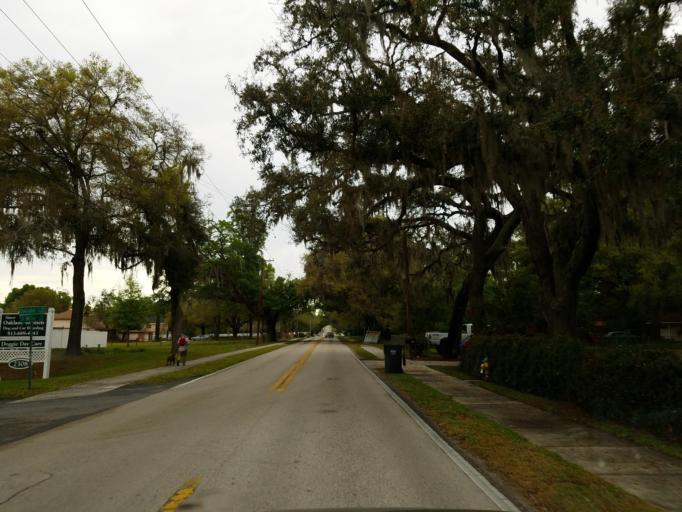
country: US
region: Florida
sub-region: Hillsborough County
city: Bloomingdale
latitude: 27.8991
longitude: -82.2442
